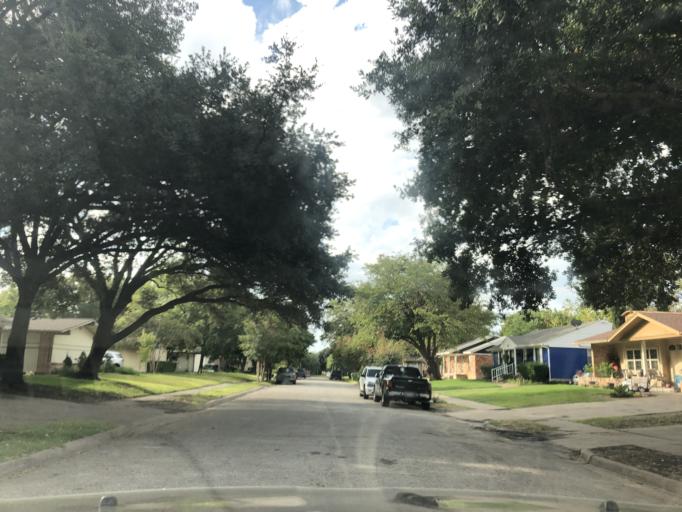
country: US
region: Texas
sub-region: Dallas County
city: Garland
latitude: 32.8903
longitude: -96.6650
